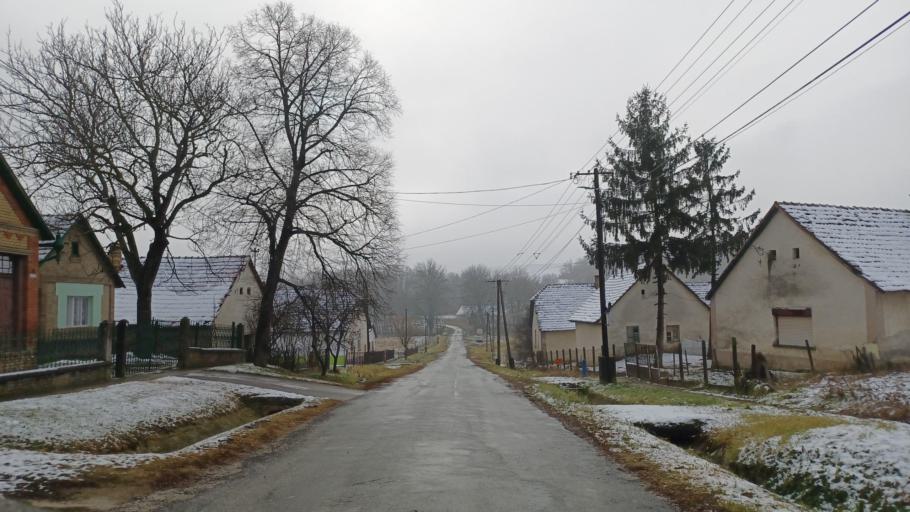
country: HU
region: Tolna
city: Gyonk
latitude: 46.5906
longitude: 18.5140
